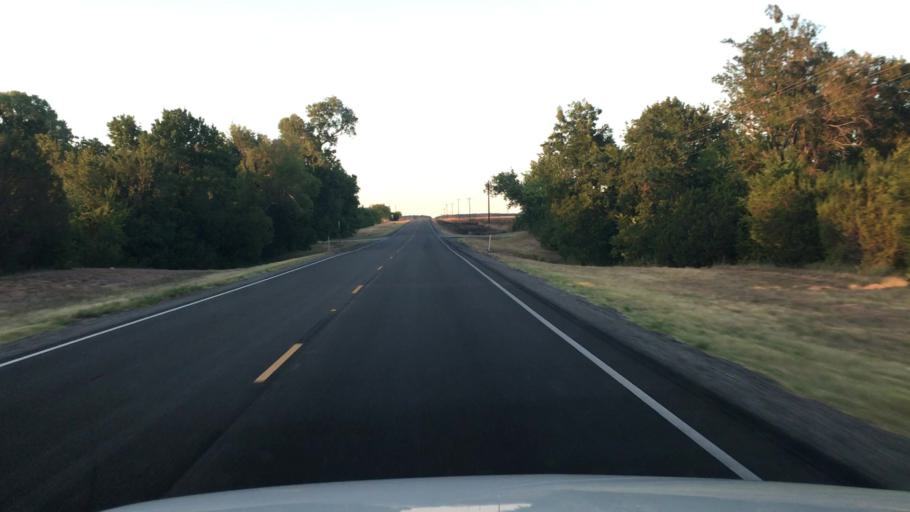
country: US
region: Texas
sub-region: Hamilton County
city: Hico
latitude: 32.0683
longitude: -97.9894
